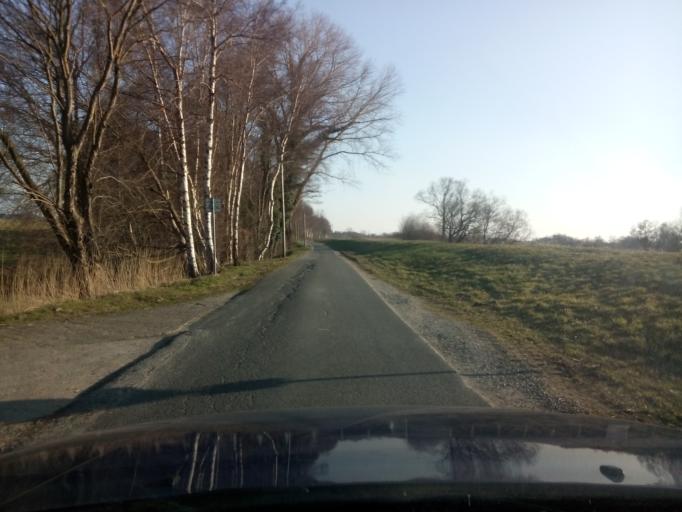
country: DE
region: Lower Saxony
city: Lilienthal
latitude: 53.1544
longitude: 8.8414
